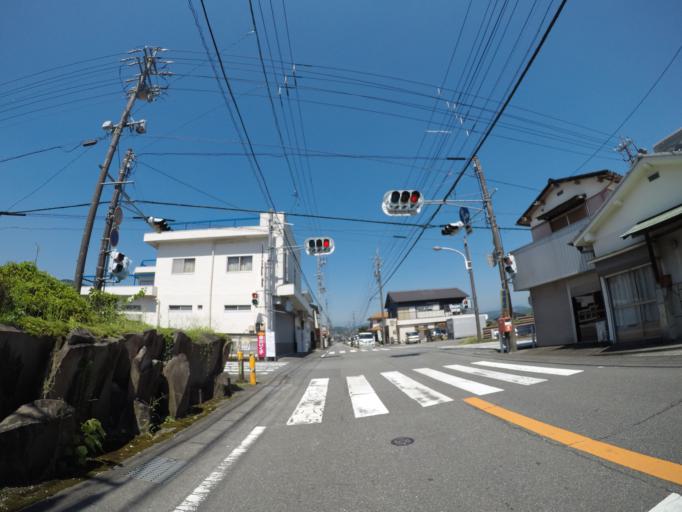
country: JP
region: Shizuoka
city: Fujinomiya
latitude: 35.1792
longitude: 138.6028
